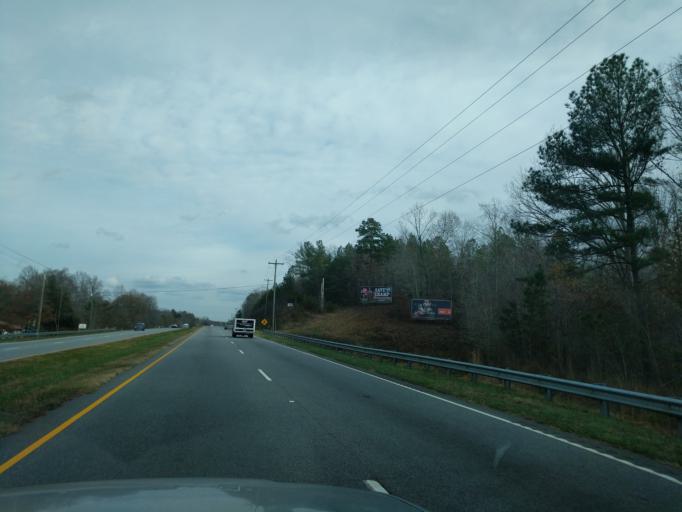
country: US
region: South Carolina
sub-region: Oconee County
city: Utica
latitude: 34.7002
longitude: -82.9273
